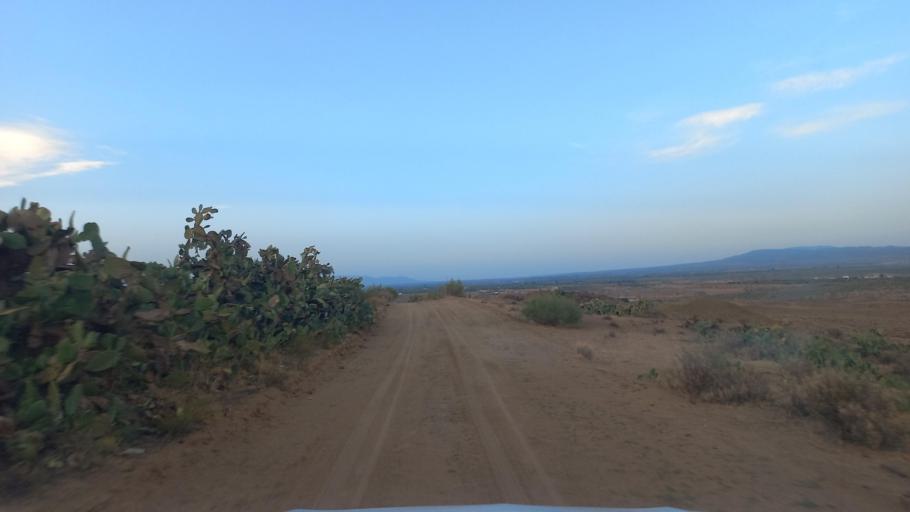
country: TN
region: Al Qasrayn
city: Kasserine
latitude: 35.1912
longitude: 9.0497
